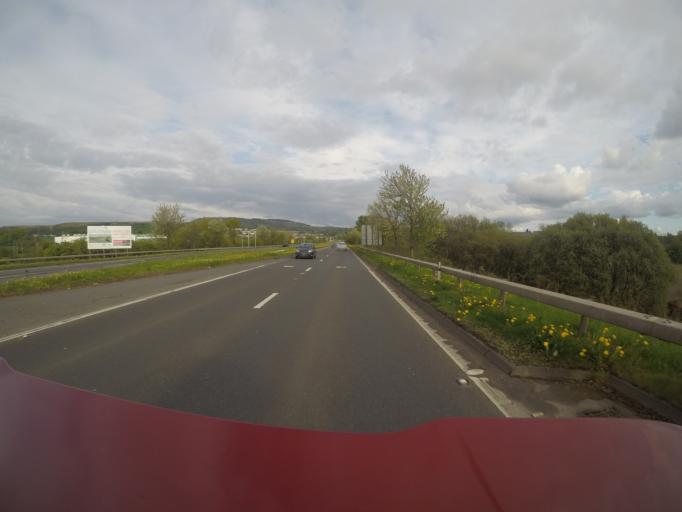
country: GB
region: Scotland
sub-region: West Dunbartonshire
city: Dumbarton
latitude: 55.9589
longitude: -4.5726
